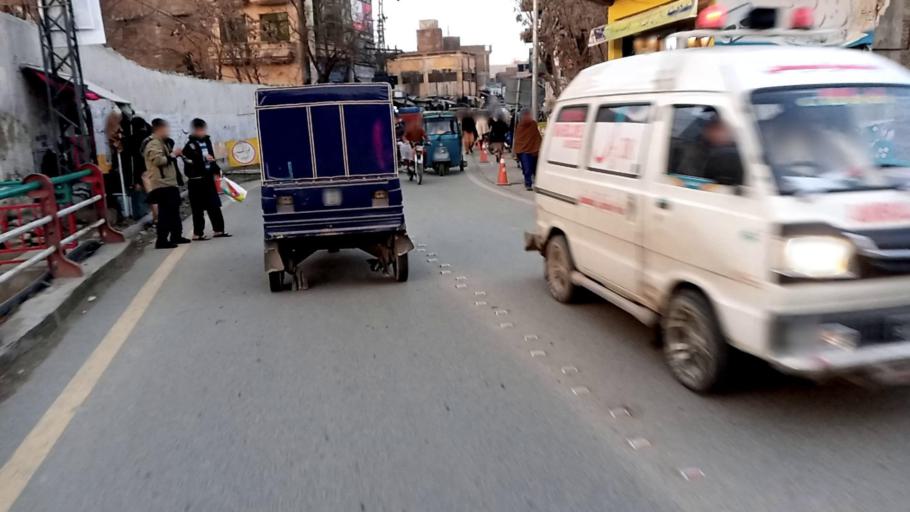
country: PK
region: Khyber Pakhtunkhwa
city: Mingora
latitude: 34.7706
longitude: 72.3584
